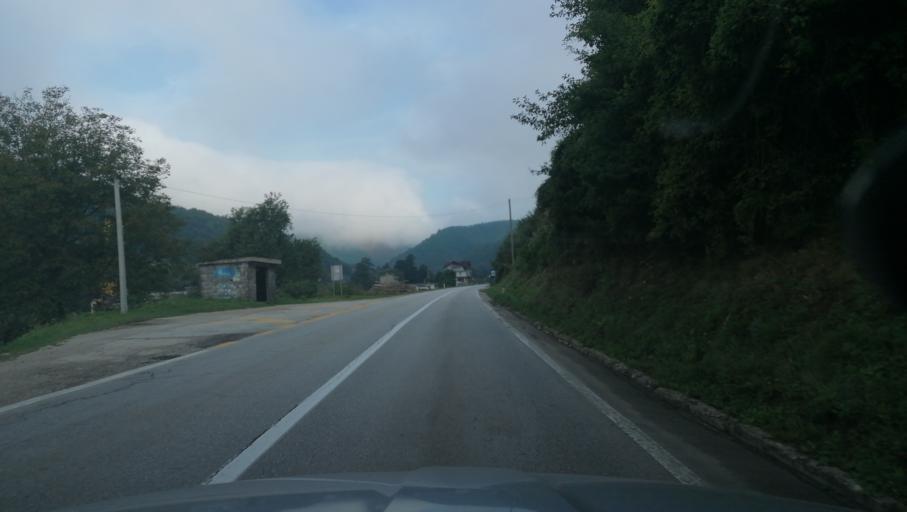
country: BA
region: Federation of Bosnia and Herzegovina
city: Donji Vakuf
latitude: 44.1757
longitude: 17.3570
